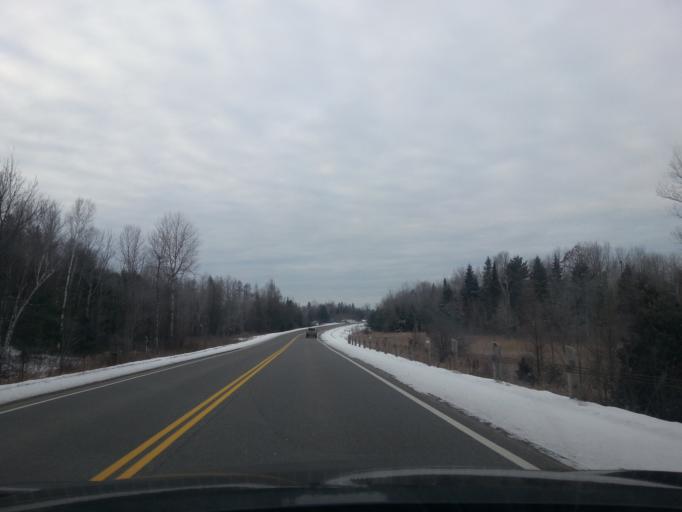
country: CA
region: Ontario
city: Perth
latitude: 44.8066
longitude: -76.6450
